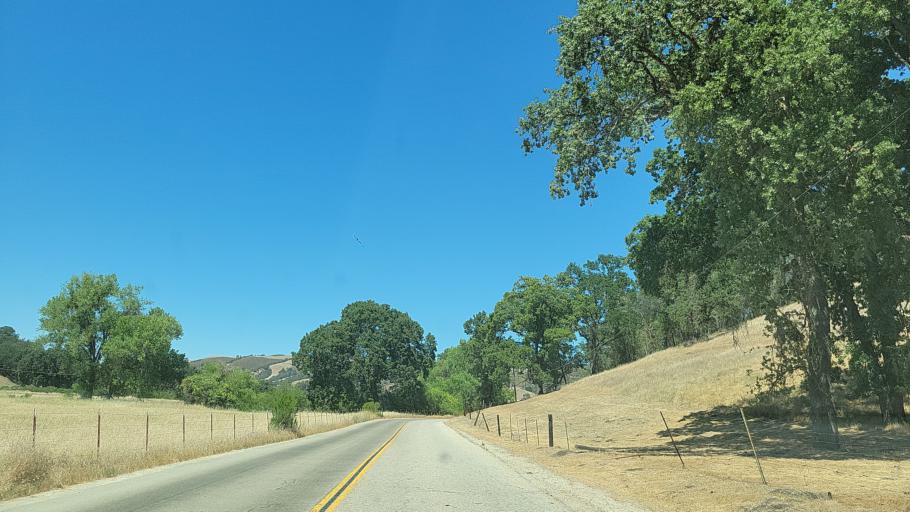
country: US
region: California
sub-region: San Luis Obispo County
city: Atascadero
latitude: 35.4579
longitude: -120.6295
